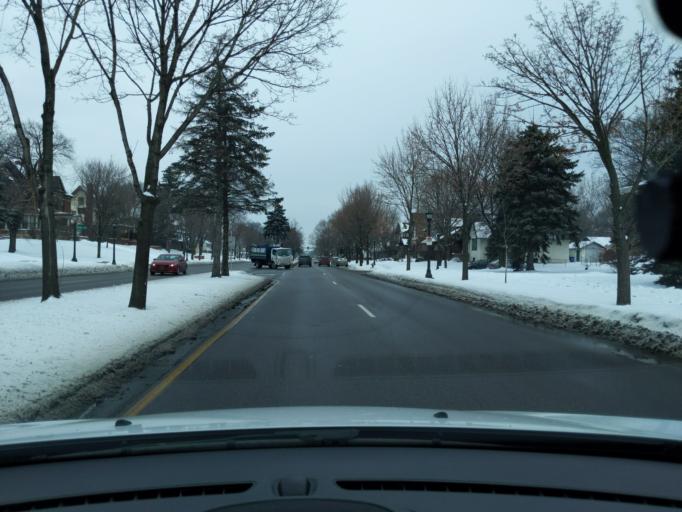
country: US
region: Minnesota
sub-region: Ramsey County
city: Falcon Heights
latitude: 44.9445
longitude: -93.1466
